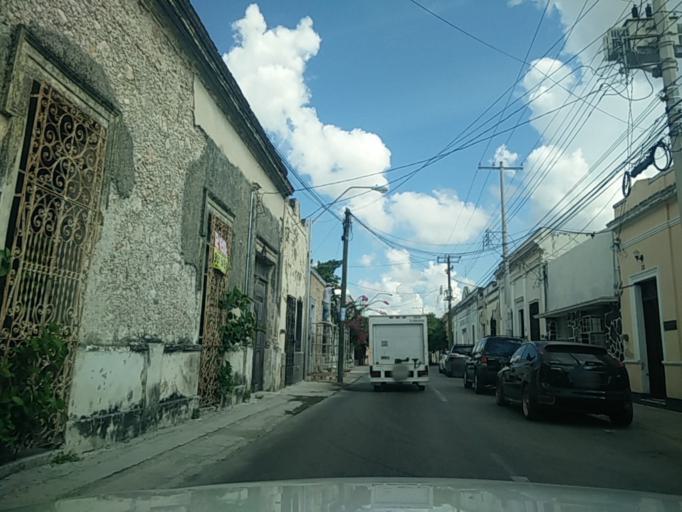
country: MX
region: Yucatan
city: Merida
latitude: 20.9729
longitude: -89.6195
